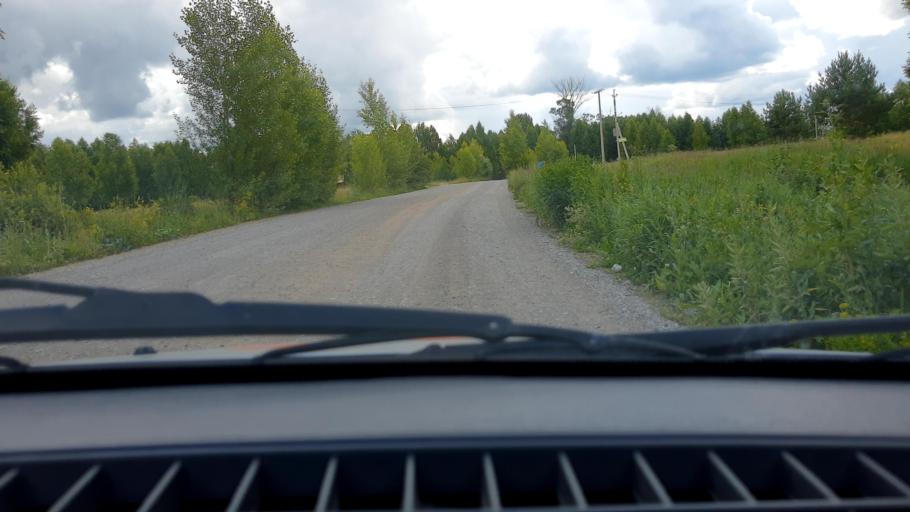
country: RU
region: Bashkortostan
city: Ufa
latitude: 54.6683
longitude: 56.0763
